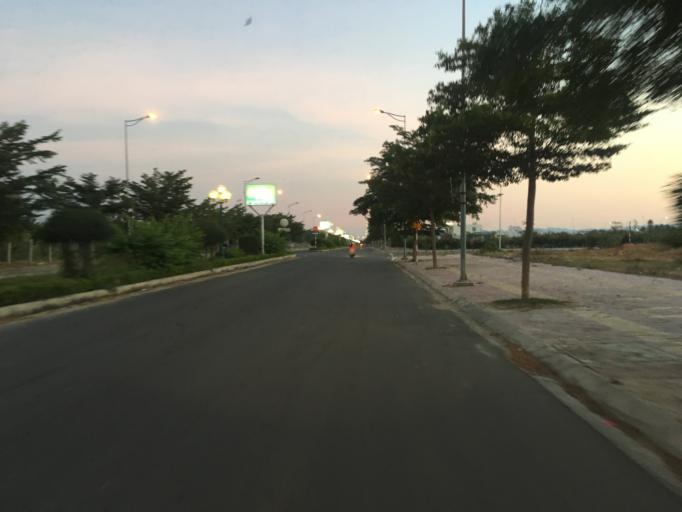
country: VN
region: Ninh Thuan
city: Phan Rang-Thap Cham
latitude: 11.5772
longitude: 109.0010
